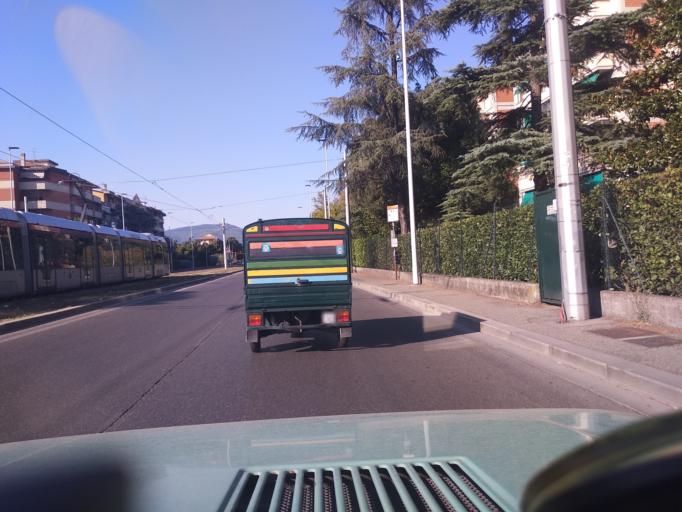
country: IT
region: Tuscany
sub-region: Province of Florence
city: Scandicci
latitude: 43.7680
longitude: 11.2098
